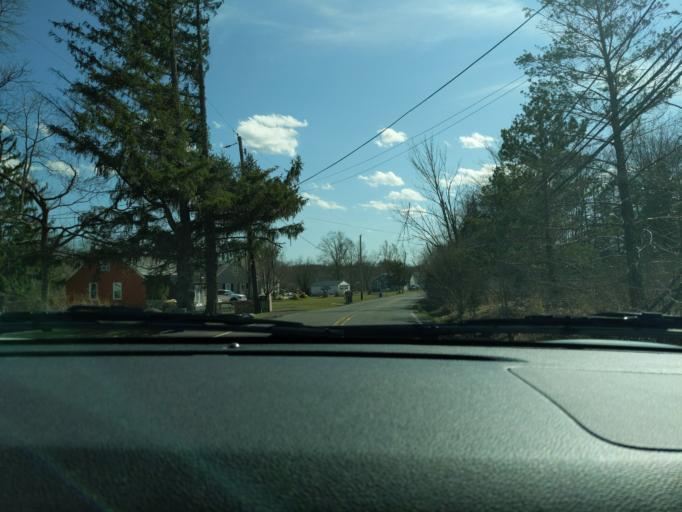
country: US
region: Pennsylvania
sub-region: Bucks County
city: Richlandtown
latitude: 40.4508
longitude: -75.3049
